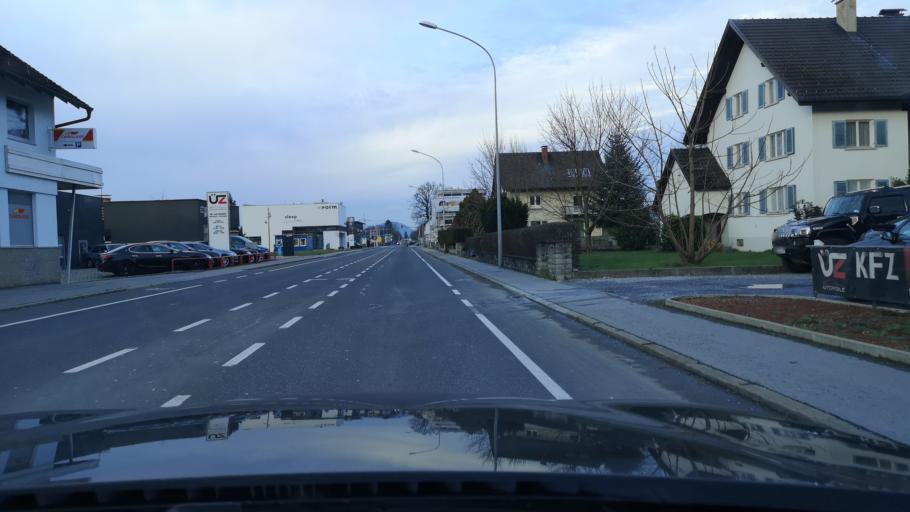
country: AT
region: Vorarlberg
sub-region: Politischer Bezirk Feldkirch
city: Rankweil
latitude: 47.2644
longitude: 9.6151
